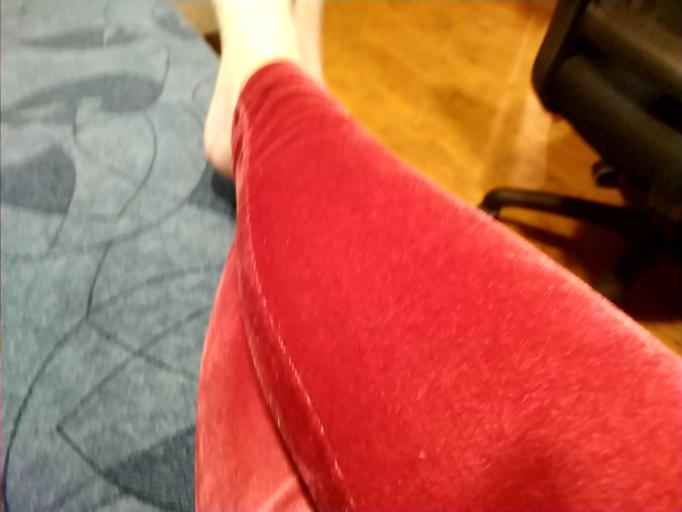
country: RU
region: Novgorod
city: Kulotino
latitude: 58.4074
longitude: 33.4472
